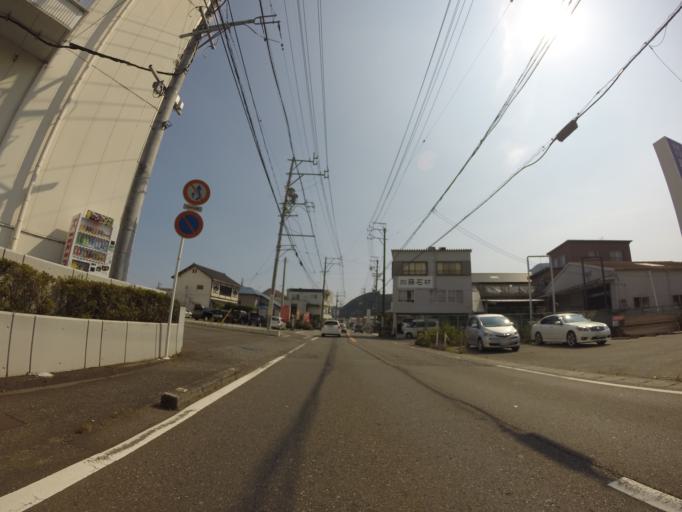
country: JP
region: Shizuoka
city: Shizuoka-shi
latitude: 35.0157
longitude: 138.3585
